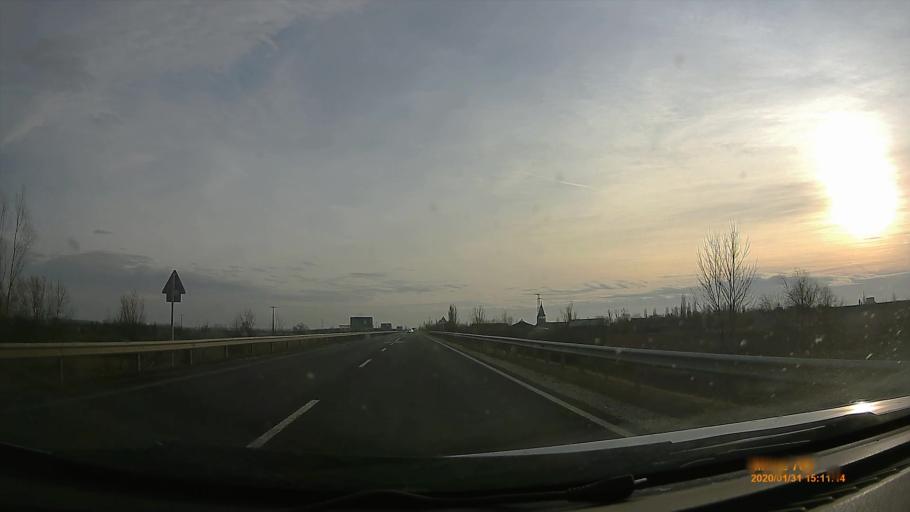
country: HU
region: Hajdu-Bihar
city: Polgar
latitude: 47.8506
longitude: 21.1510
